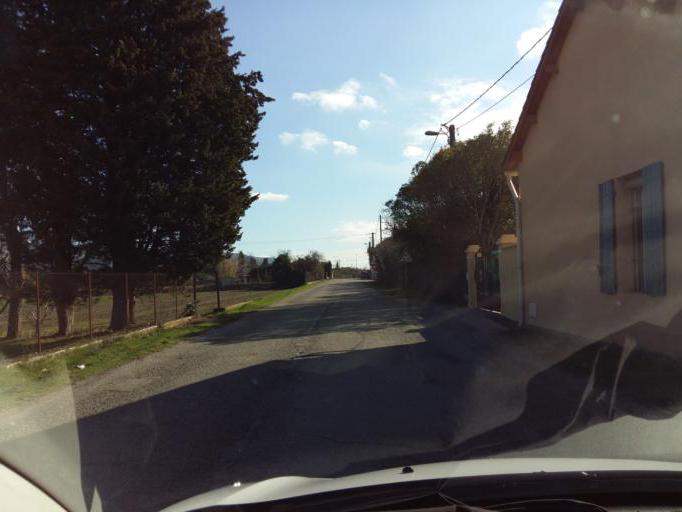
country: FR
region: Provence-Alpes-Cote d'Azur
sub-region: Departement du Vaucluse
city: Cavaillon
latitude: 43.8210
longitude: 5.0507
